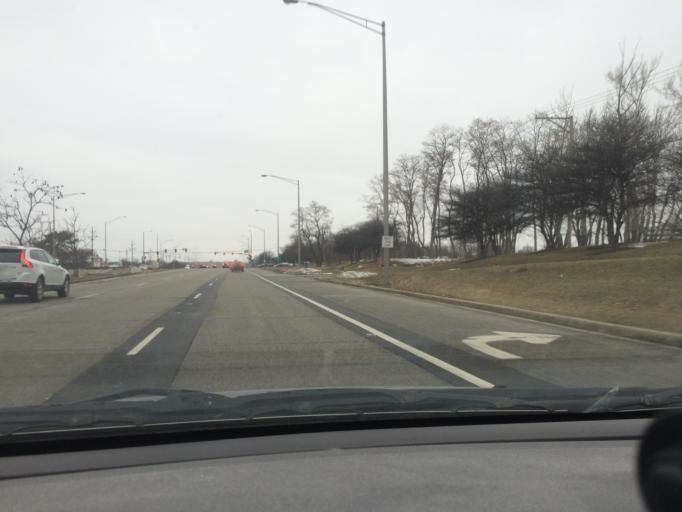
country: US
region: Illinois
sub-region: Cook County
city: Hoffman Estates
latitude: 42.0388
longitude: -88.0423
